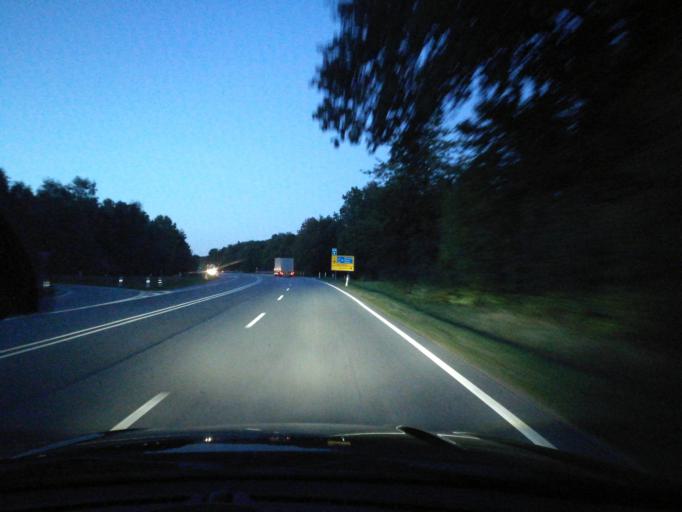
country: DE
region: Bavaria
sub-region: Lower Bavaria
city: Bad Abbach
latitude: 48.9424
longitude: 12.0447
